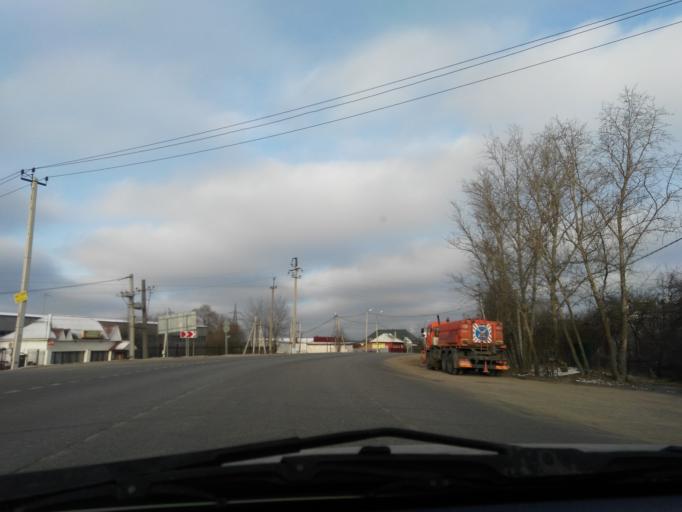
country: RU
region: Moskovskaya
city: Selyatino
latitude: 55.2768
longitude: 37.1145
